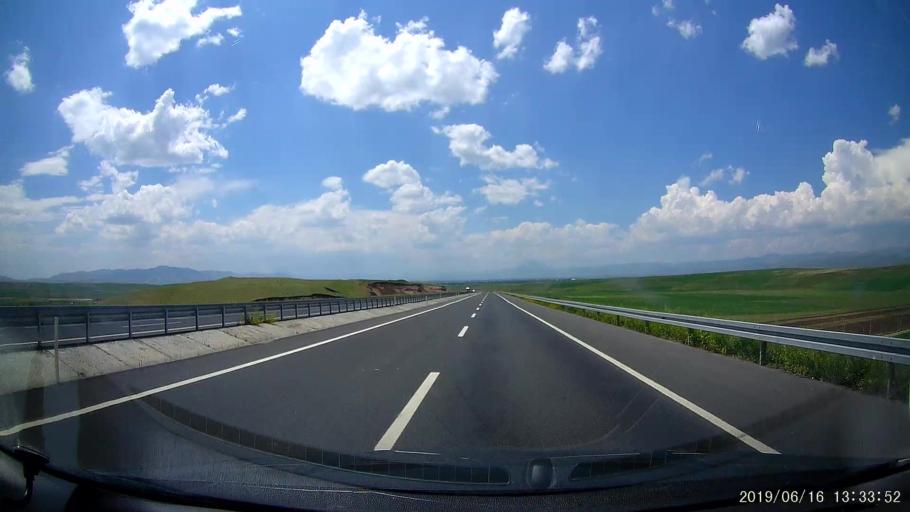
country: TR
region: Agri
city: Agri
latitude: 39.7092
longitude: 43.1429
